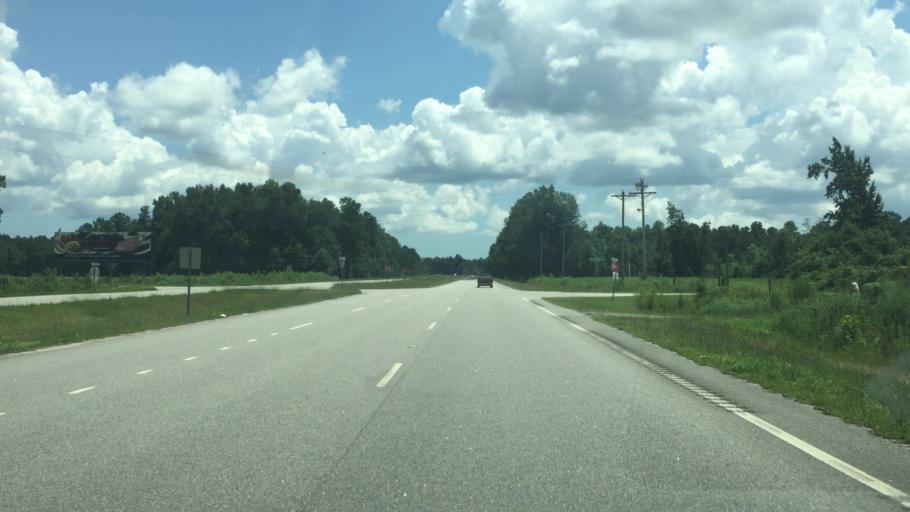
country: US
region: South Carolina
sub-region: Horry County
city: Loris
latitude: 34.0256
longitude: -78.7995
